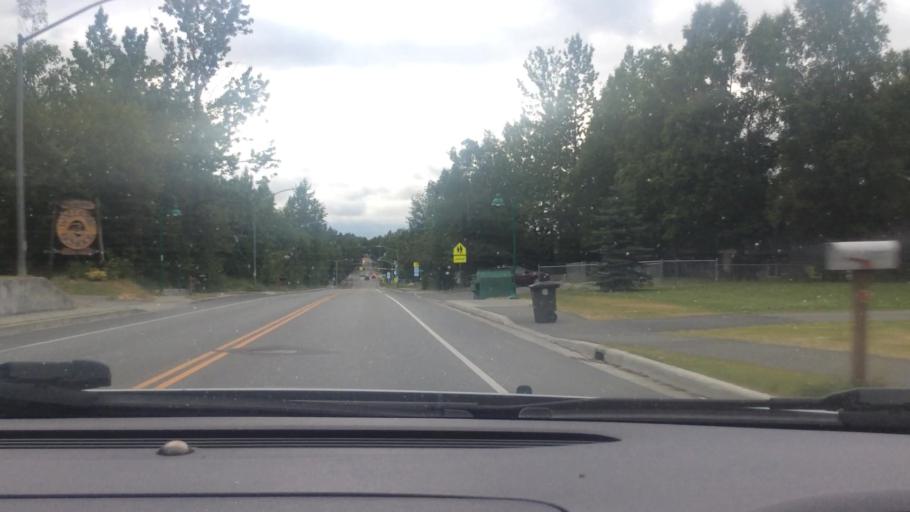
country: US
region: Alaska
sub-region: Anchorage Municipality
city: Anchorage
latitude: 61.1909
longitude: -149.7634
